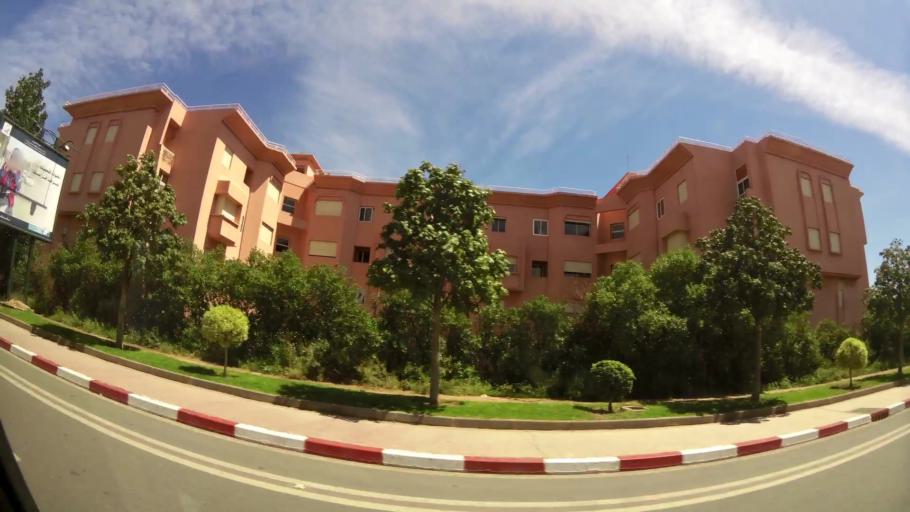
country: MA
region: Marrakech-Tensift-Al Haouz
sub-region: Marrakech
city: Marrakesh
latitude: 31.6734
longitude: -8.0049
